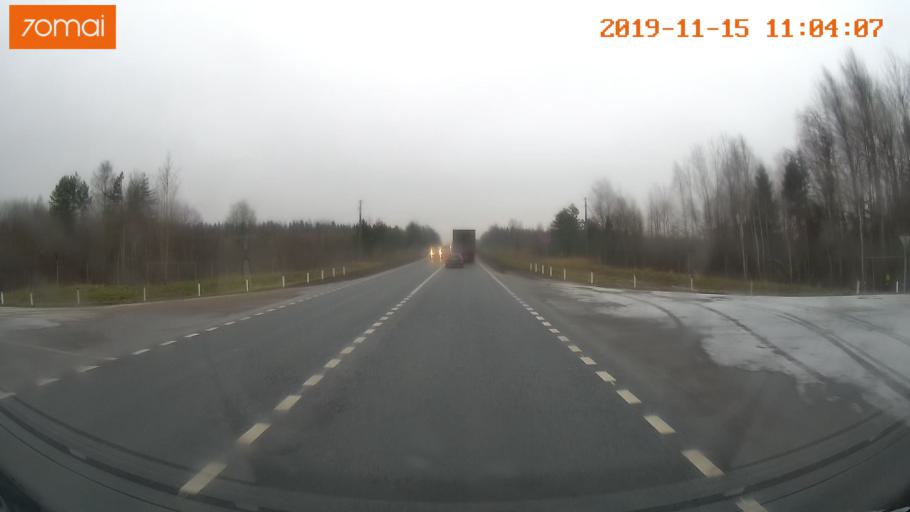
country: RU
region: Vologda
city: Chebsara
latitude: 59.1216
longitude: 38.9764
